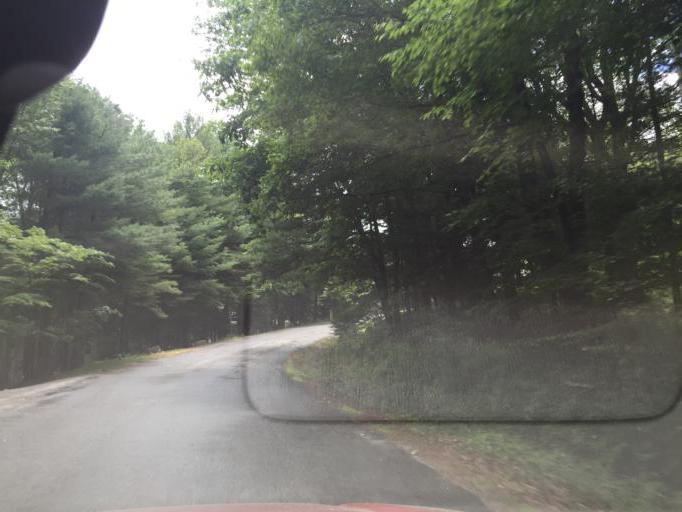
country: US
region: Connecticut
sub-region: Litchfield County
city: Litchfield
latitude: 41.8098
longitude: -73.2589
